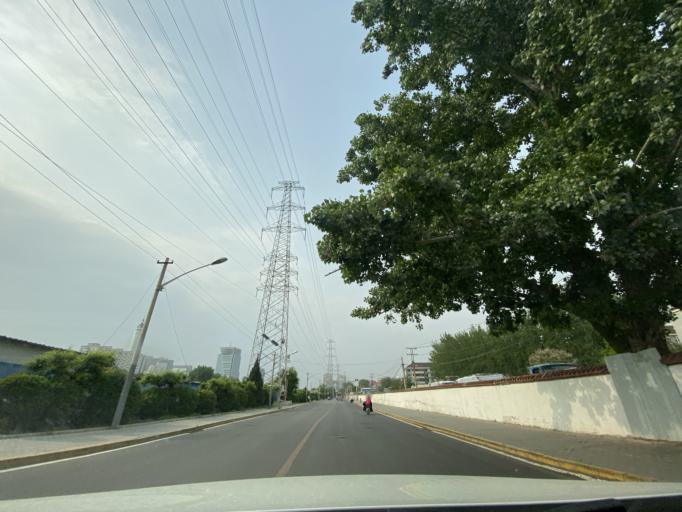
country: CN
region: Beijing
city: Haidian
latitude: 39.9779
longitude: 116.3351
